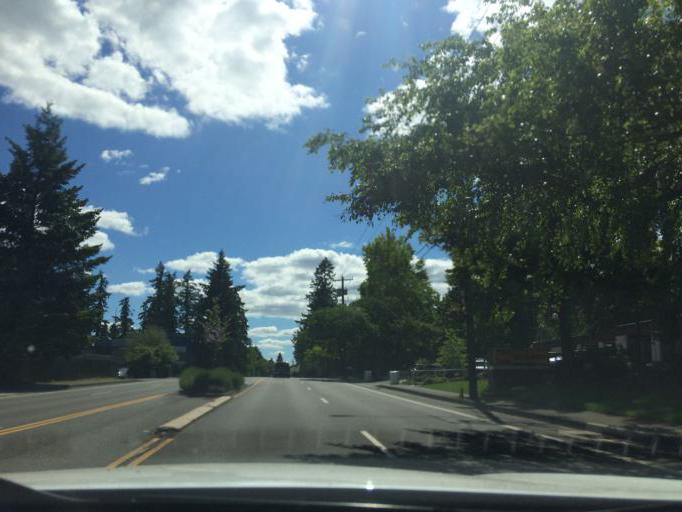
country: US
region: Oregon
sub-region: Washington County
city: Durham
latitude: 45.4018
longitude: -122.7343
